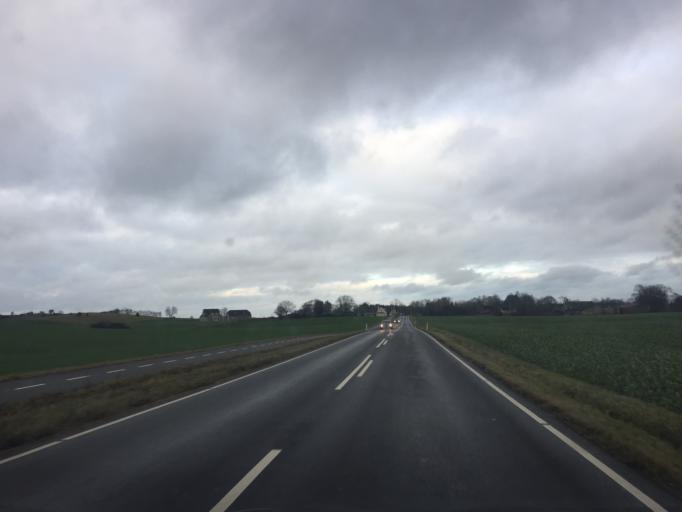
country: DK
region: Zealand
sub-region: Holbaek Kommune
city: Tollose
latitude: 55.6037
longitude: 11.7035
